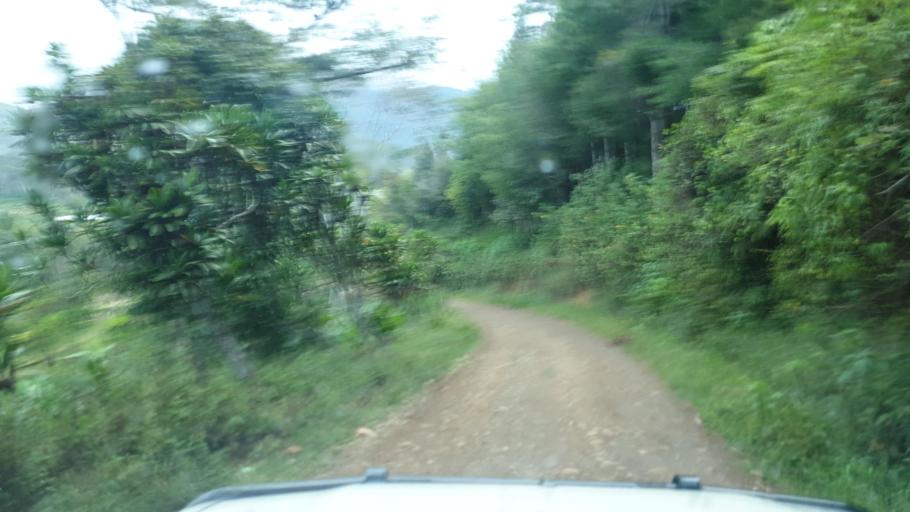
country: PG
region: Eastern Highlands
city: Goroka
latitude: -5.9654
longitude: 145.2747
